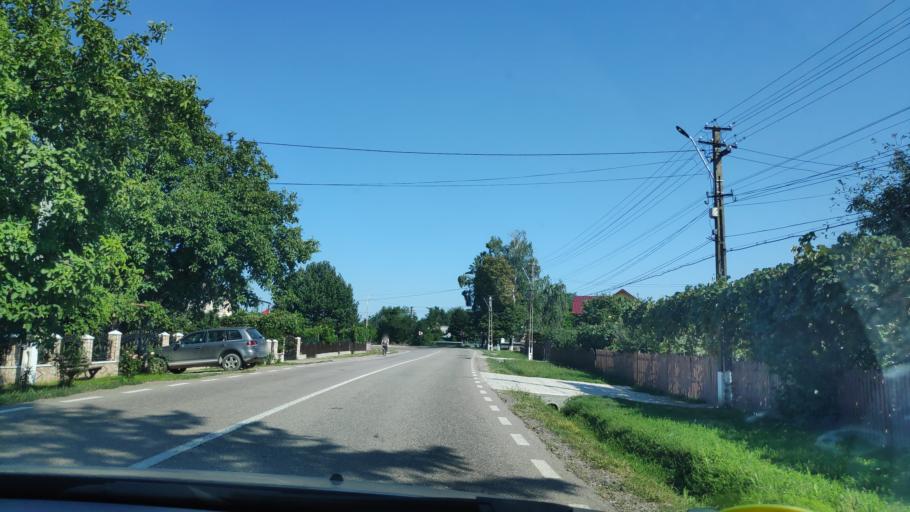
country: RO
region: Suceava
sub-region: Comuna Boroaia
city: Boroaia
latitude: 47.3525
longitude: 26.3387
